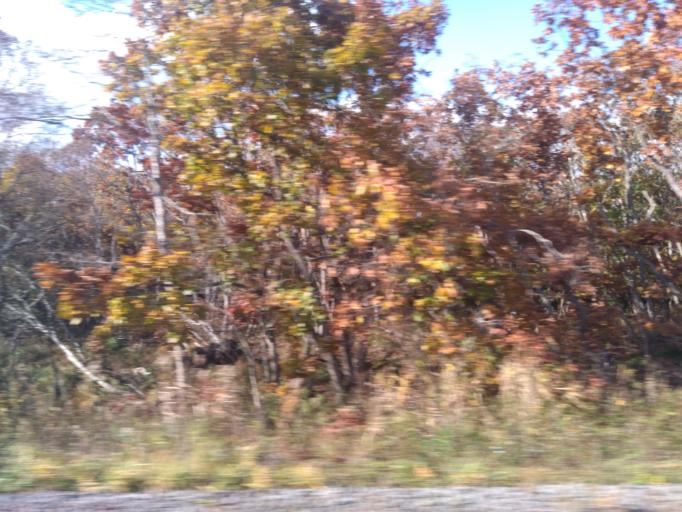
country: JP
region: Hokkaido
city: Shiraoi
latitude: 42.5273
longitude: 141.3157
